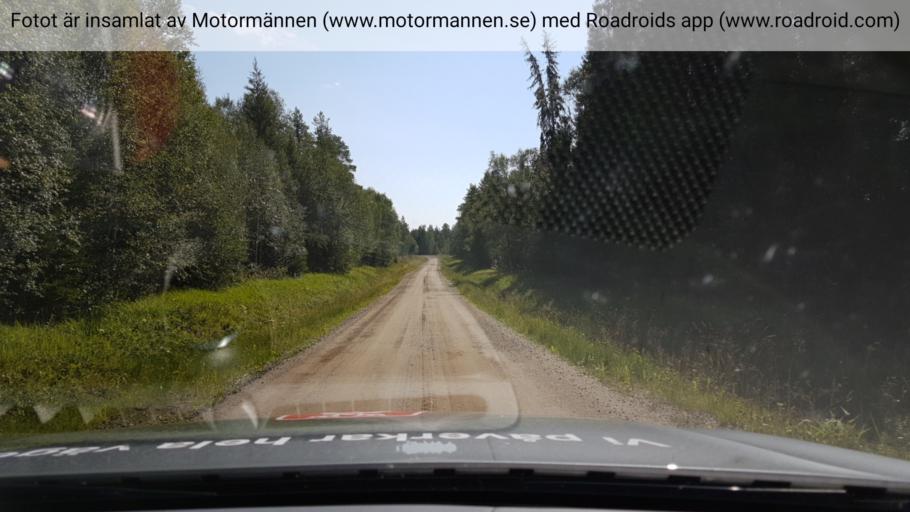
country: SE
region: Jaemtland
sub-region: Stroemsunds Kommun
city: Stroemsund
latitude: 63.3205
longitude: 15.4741
